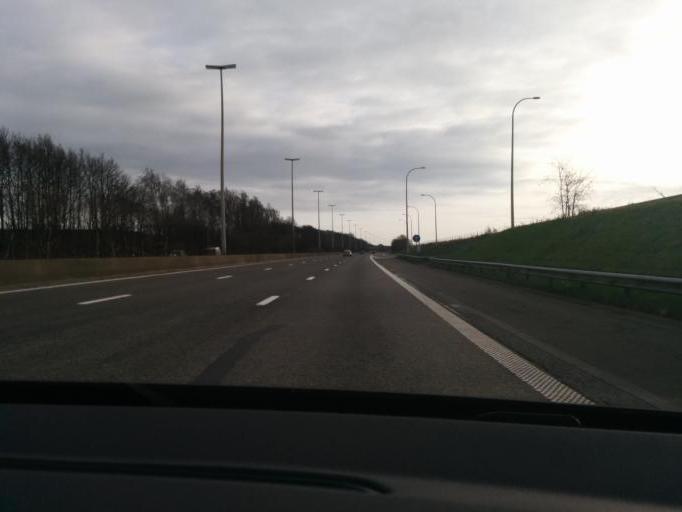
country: BE
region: Flanders
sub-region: Provincie Vlaams-Brabant
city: Tienen
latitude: 50.7793
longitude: 4.9240
